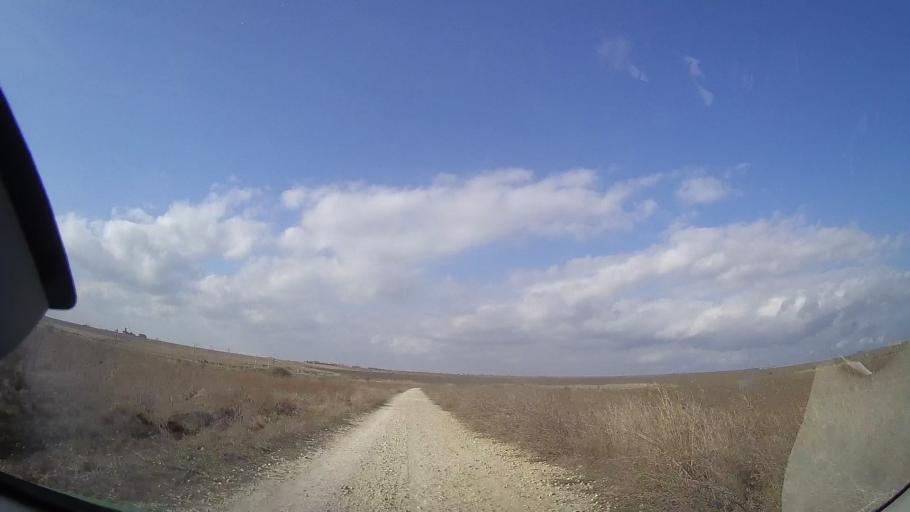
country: RO
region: Constanta
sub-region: Comuna Douazeci si Trei August
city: Douazeci si Trei August
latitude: 43.9077
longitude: 28.6108
